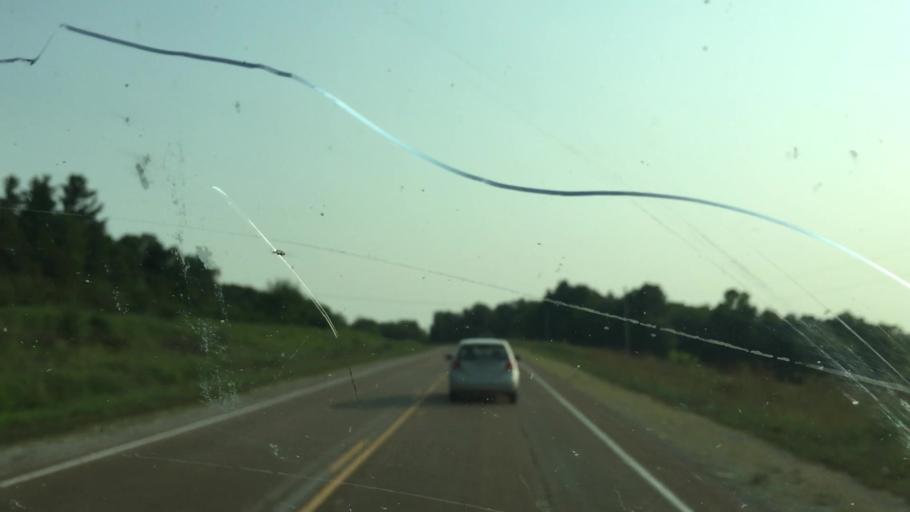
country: US
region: Missouri
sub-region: Pulaski County
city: Richland
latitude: 37.7882
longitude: -92.4095
